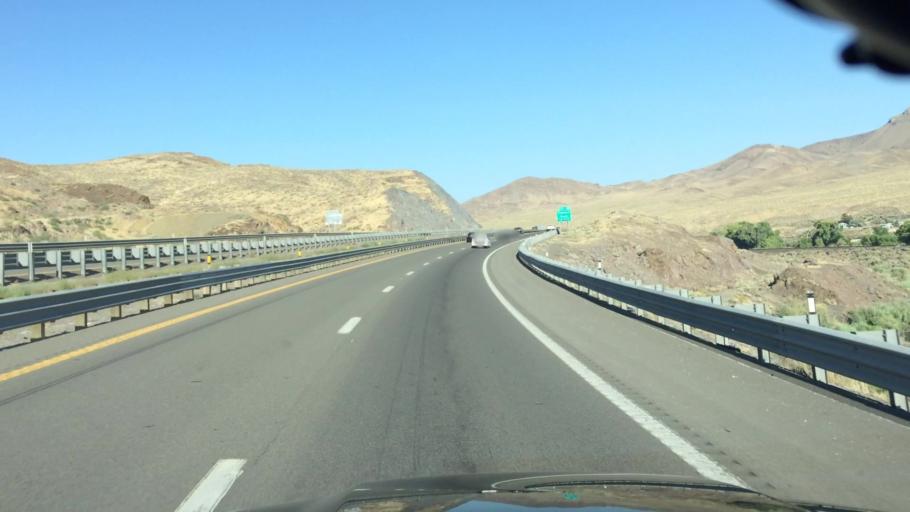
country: US
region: Nevada
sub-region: Lyon County
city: Fernley
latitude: 39.5910
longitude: -119.3817
